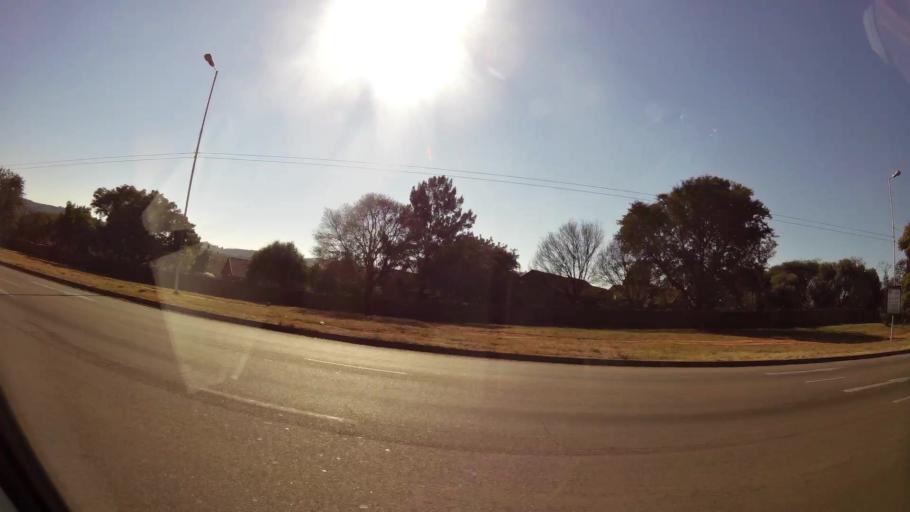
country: ZA
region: Gauteng
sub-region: City of Tshwane Metropolitan Municipality
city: Pretoria
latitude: -25.7868
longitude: 28.3072
